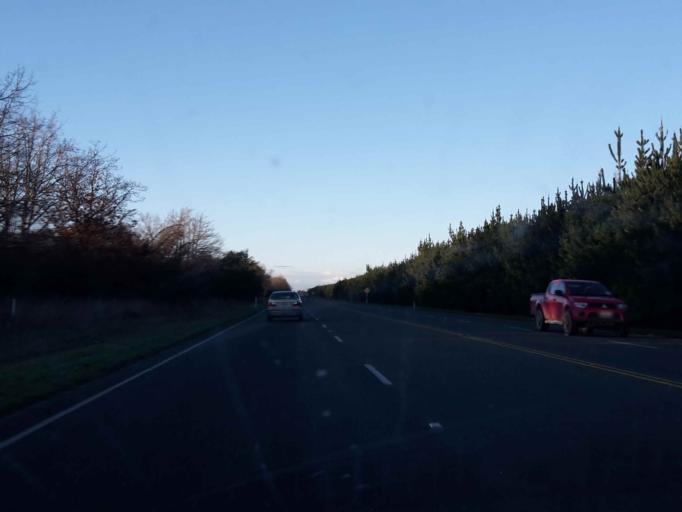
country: NZ
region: Canterbury
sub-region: Selwyn District
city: Burnham
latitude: -43.6315
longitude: 172.2718
